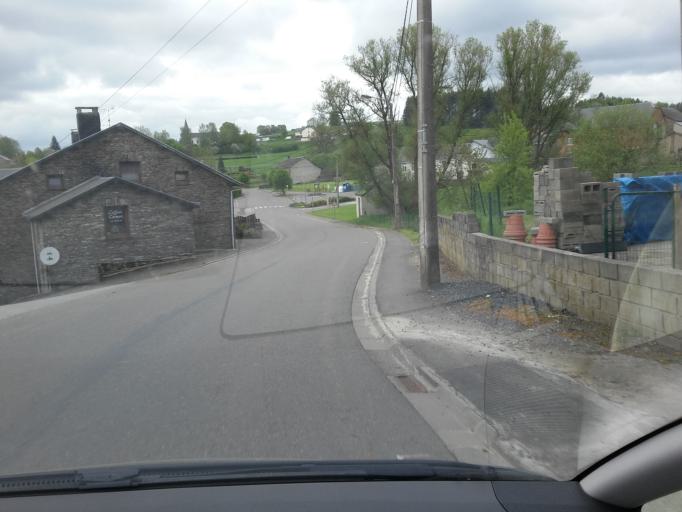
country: BE
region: Wallonia
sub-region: Province du Luxembourg
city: Bertrix
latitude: 49.8218
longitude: 5.3240
